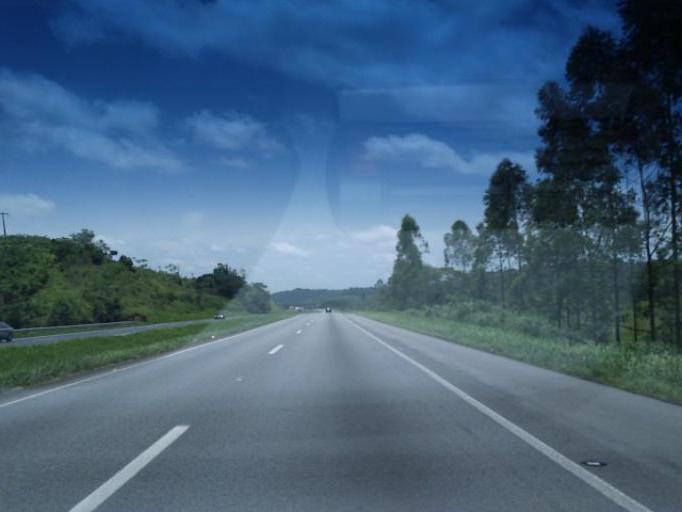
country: BR
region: Sao Paulo
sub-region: Registro
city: Registro
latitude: -24.4202
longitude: -47.7707
